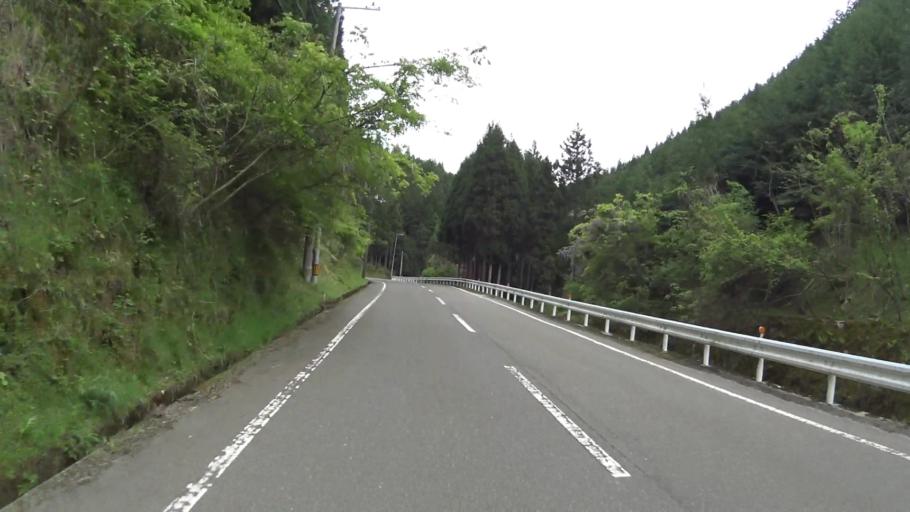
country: JP
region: Kyoto
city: Kameoka
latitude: 35.1356
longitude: 135.6168
